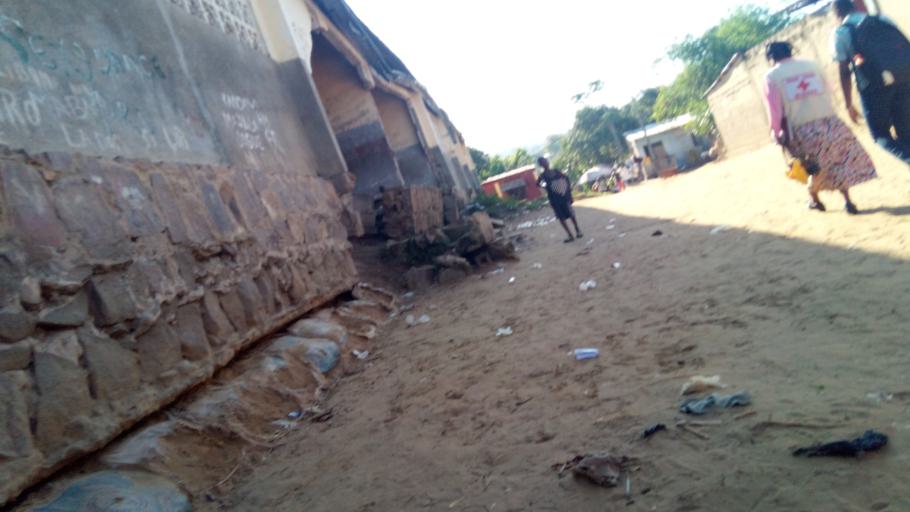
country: CD
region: Kinshasa
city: Kinshasa
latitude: -4.3698
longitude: 15.2770
